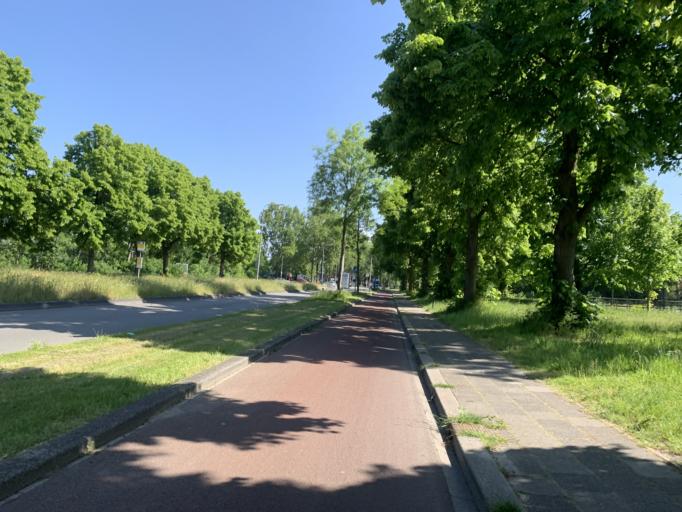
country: NL
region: Groningen
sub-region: Gemeente Groningen
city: Groningen
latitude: 53.2178
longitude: 6.5295
